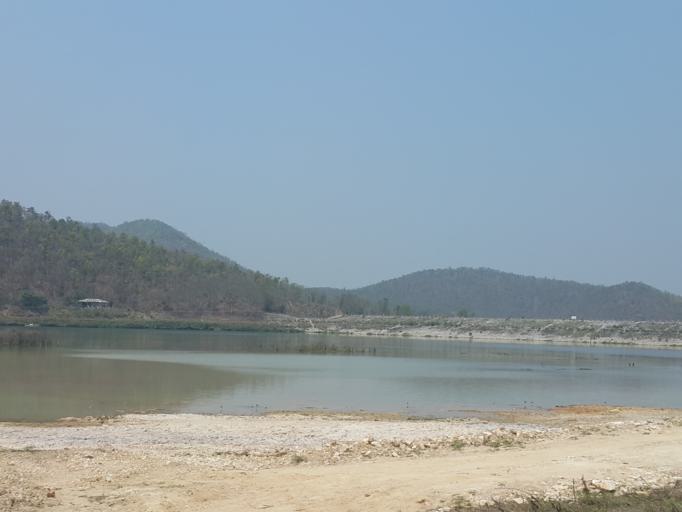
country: TH
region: Chiang Mai
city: Mae On
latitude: 18.7023
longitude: 99.2058
